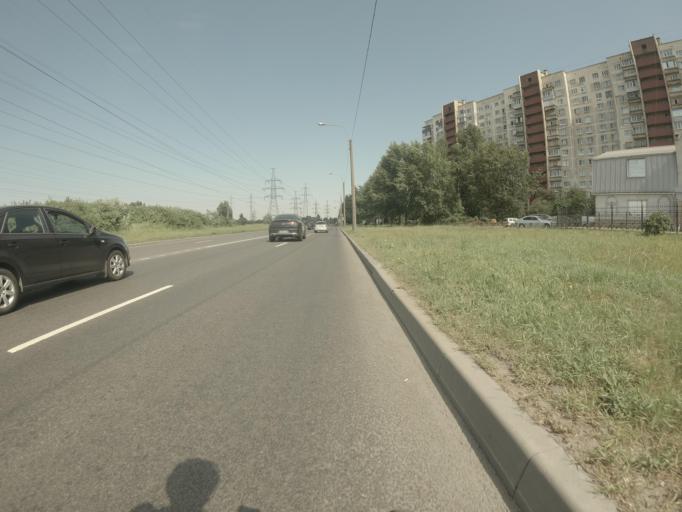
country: RU
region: St.-Petersburg
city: Krasnogvargeisky
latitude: 59.9494
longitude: 30.4609
